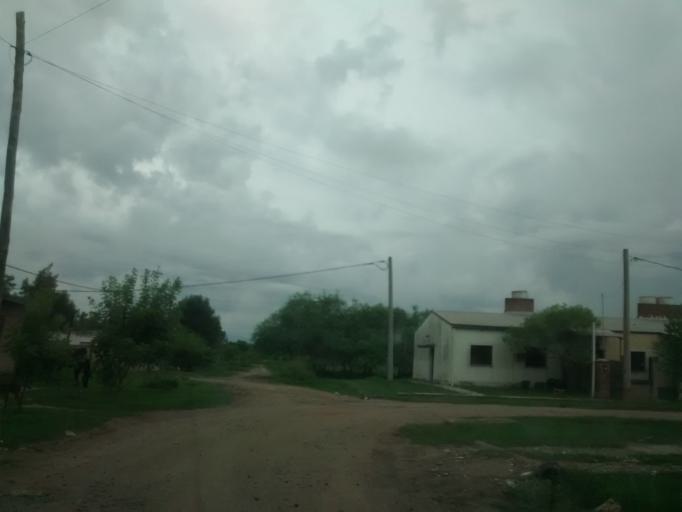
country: AR
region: Chaco
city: Puerto Tirol
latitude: -27.3749
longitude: -59.0981
